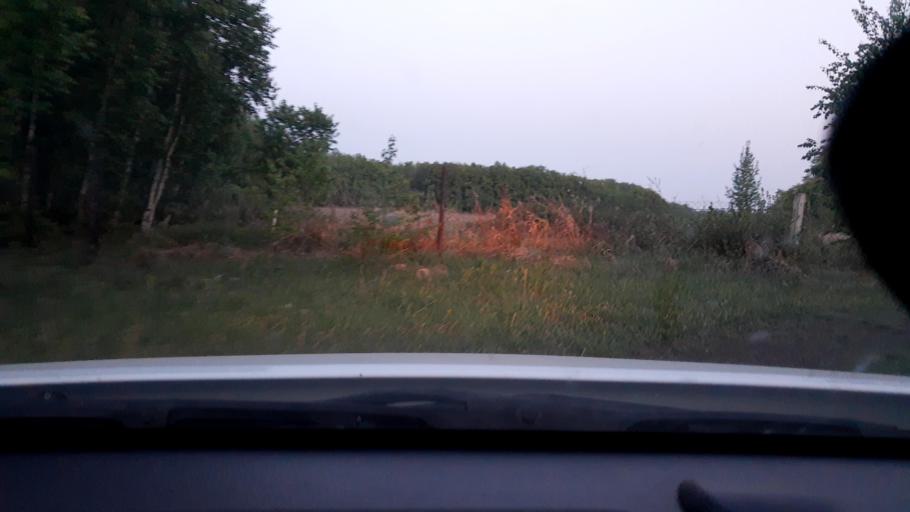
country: RU
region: Bashkortostan
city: Avdon
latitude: 54.5327
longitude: 55.8238
